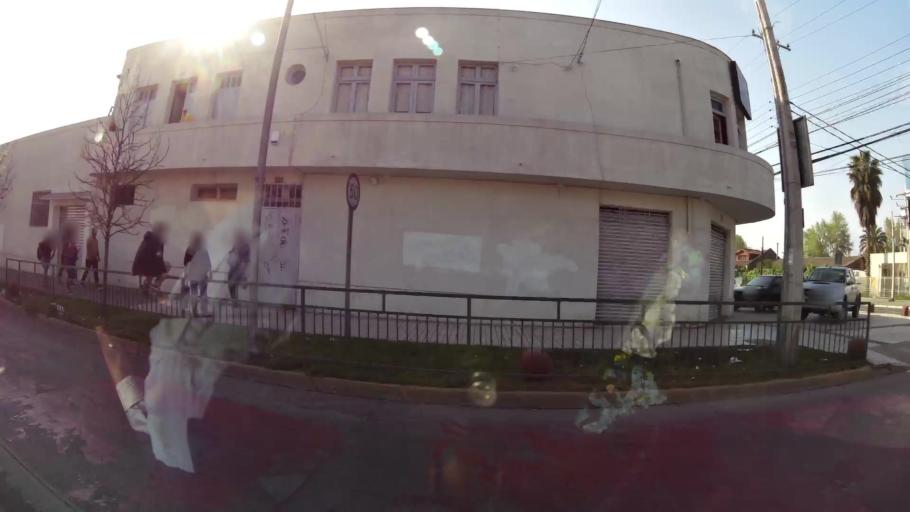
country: CL
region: Santiago Metropolitan
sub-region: Provincia de Santiago
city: Santiago
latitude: -33.3990
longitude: -70.6727
